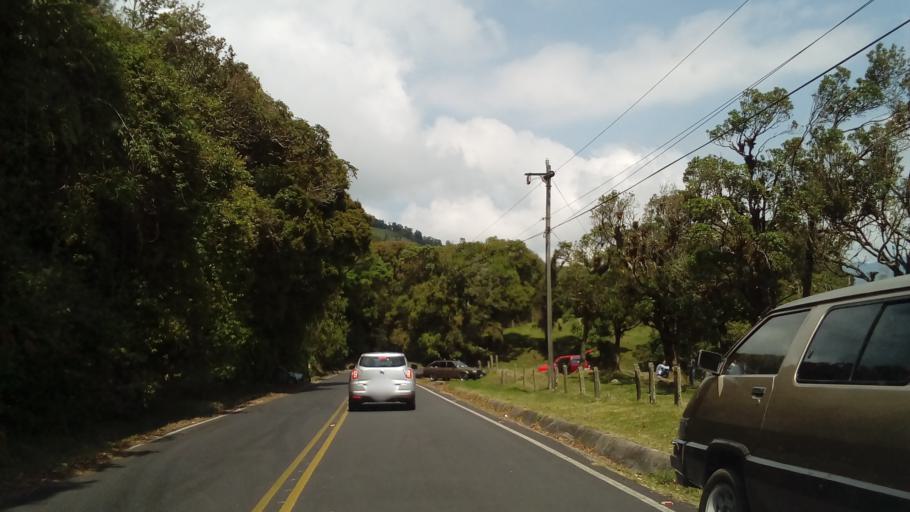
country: CR
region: Alajuela
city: Sabanilla
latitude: 10.1644
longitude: -84.2258
